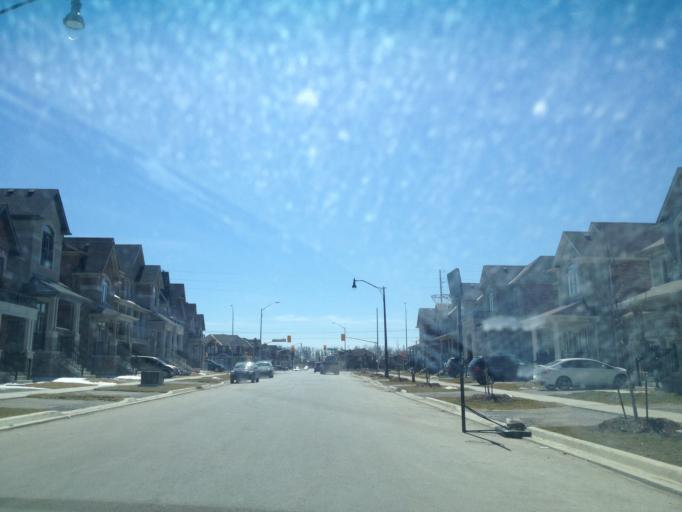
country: CA
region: Ontario
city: Brampton
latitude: 43.7027
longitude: -79.8519
